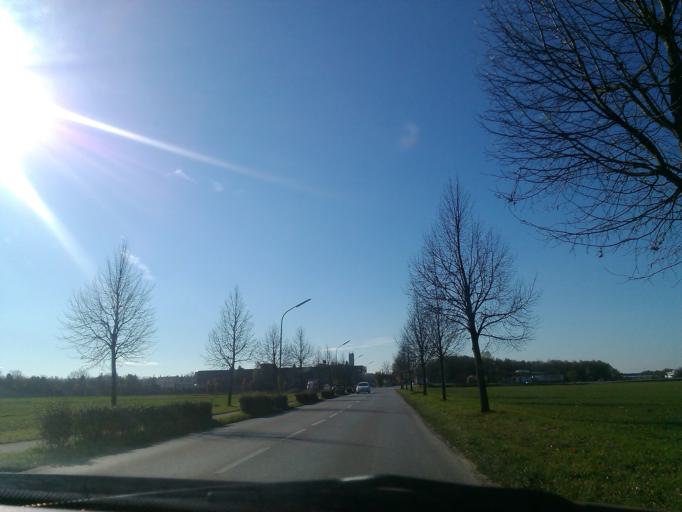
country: DE
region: Bavaria
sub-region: Upper Bavaria
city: Olching
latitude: 48.2250
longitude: 11.3403
